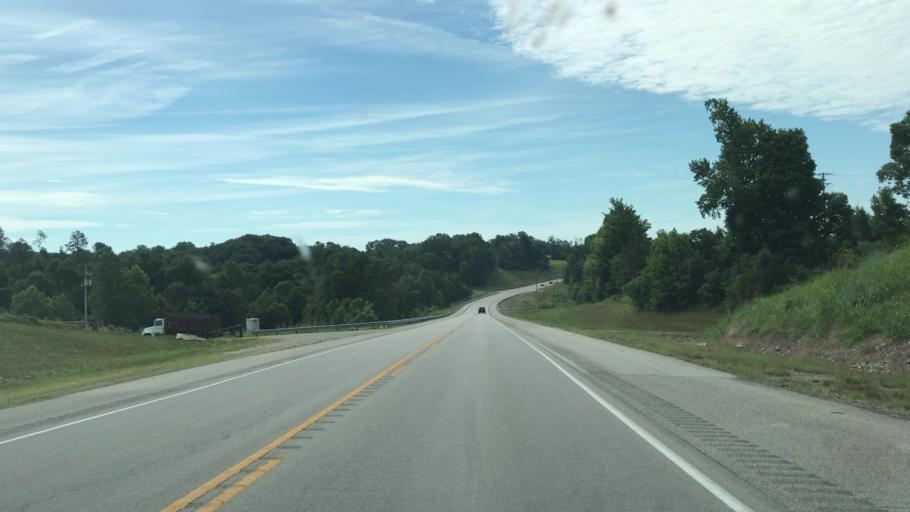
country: US
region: Kentucky
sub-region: Edmonson County
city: Brownsville
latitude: 37.1646
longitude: -86.2261
